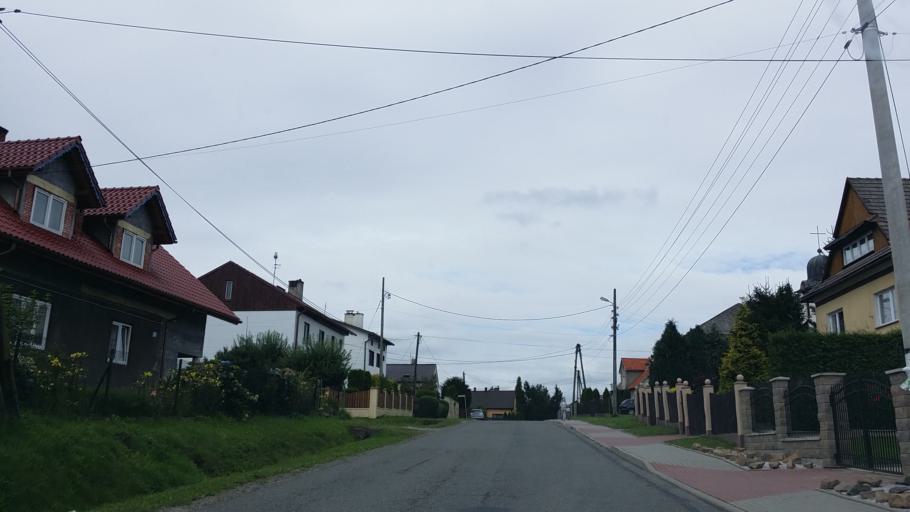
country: PL
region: Lesser Poland Voivodeship
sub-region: Powiat wadowicki
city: Tomice
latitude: 49.8974
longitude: 19.4793
